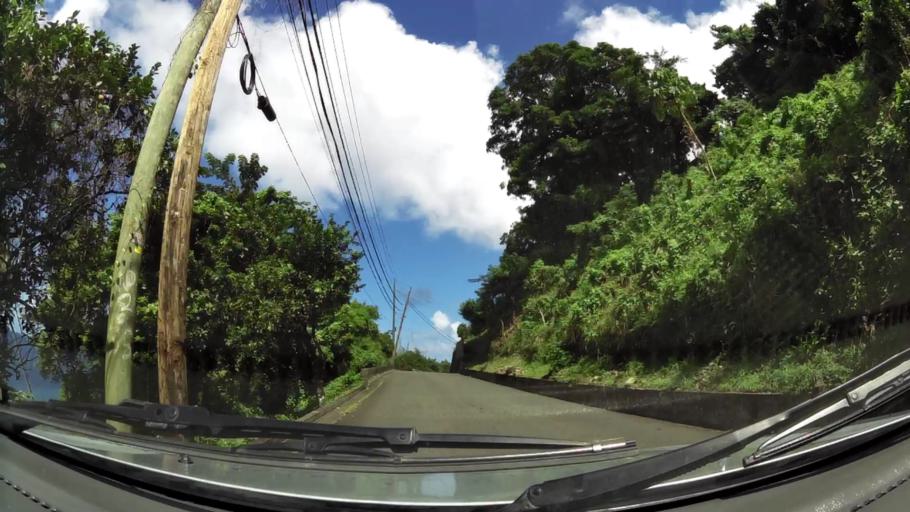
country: GD
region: Saint Mark
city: Victoria
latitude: 12.1916
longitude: -61.7147
